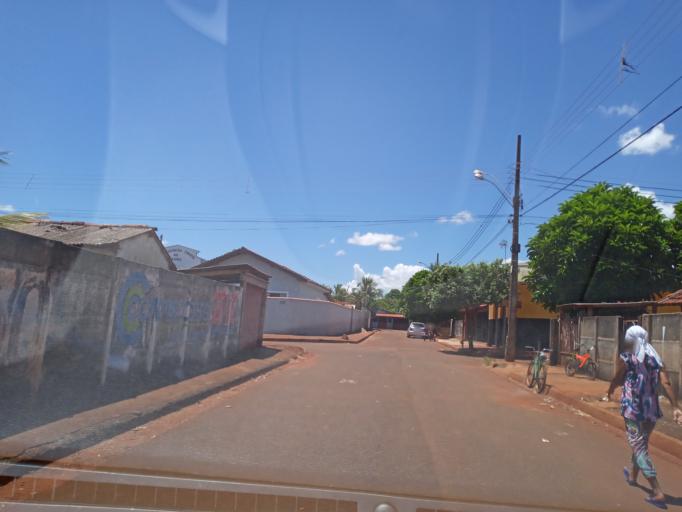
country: BR
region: Minas Gerais
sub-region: Centralina
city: Centralina
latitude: -18.5826
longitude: -49.2076
